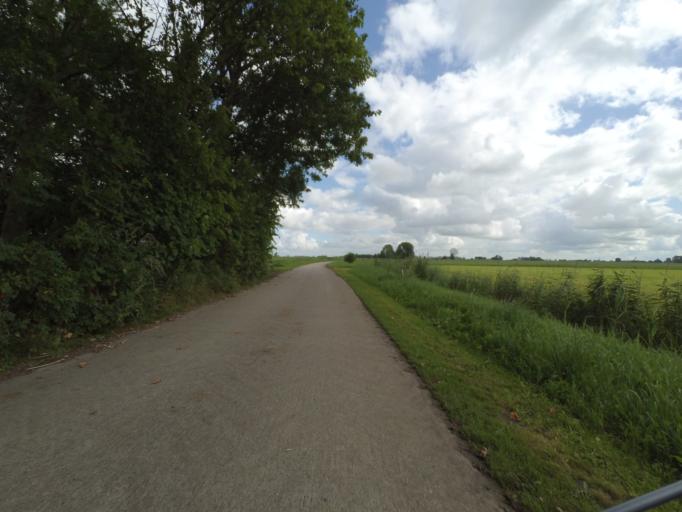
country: NL
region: Friesland
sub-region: Gemeente Kollumerland en Nieuwkruisland
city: Kollum
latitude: 53.2769
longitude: 6.1996
